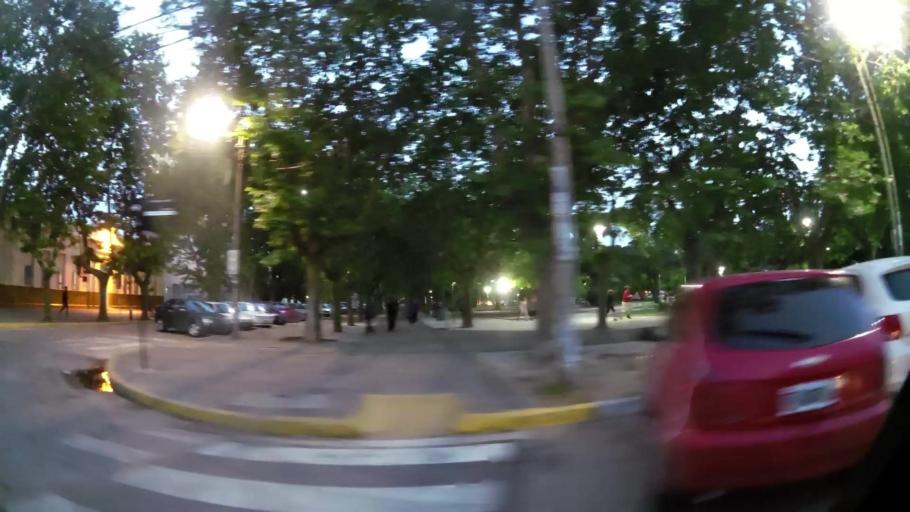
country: AR
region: Buenos Aires
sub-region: Partido de Quilmes
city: Quilmes
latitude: -34.8041
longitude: -58.2802
